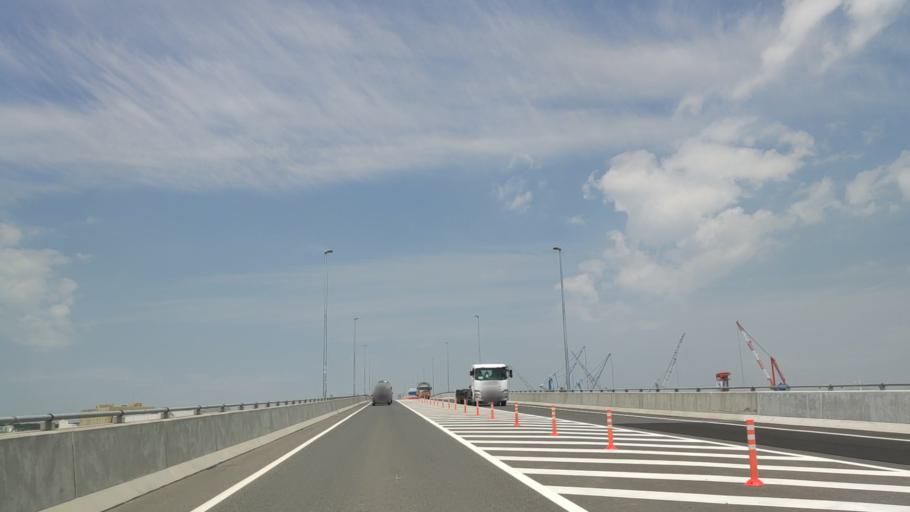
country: JP
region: Kanagawa
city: Yokohama
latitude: 35.4101
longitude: 139.6828
